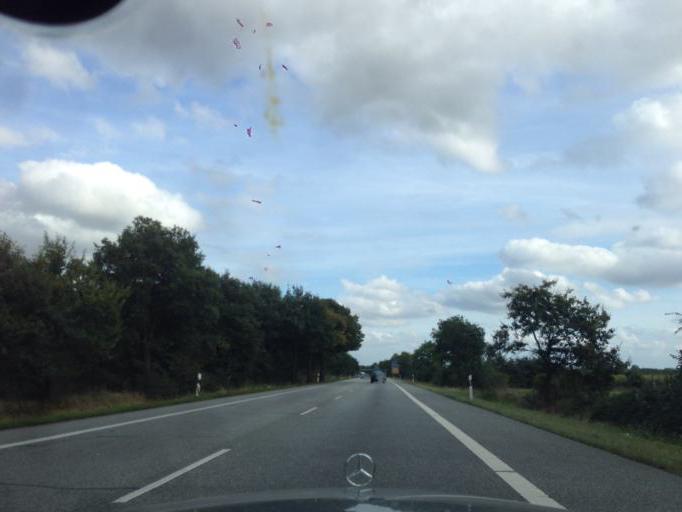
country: DE
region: Schleswig-Holstein
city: Wahlstedt
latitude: 53.9753
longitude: 10.2203
